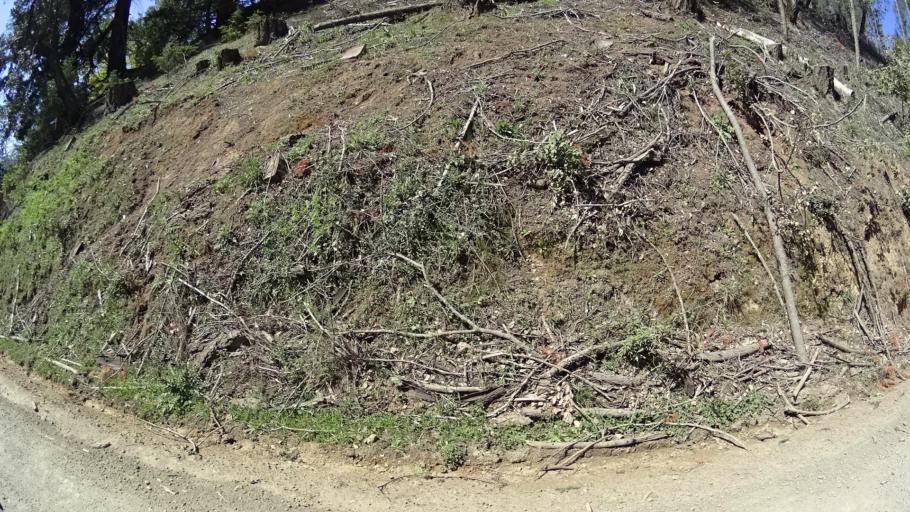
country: US
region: California
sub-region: Humboldt County
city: Redway
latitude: 40.0194
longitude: -123.6239
